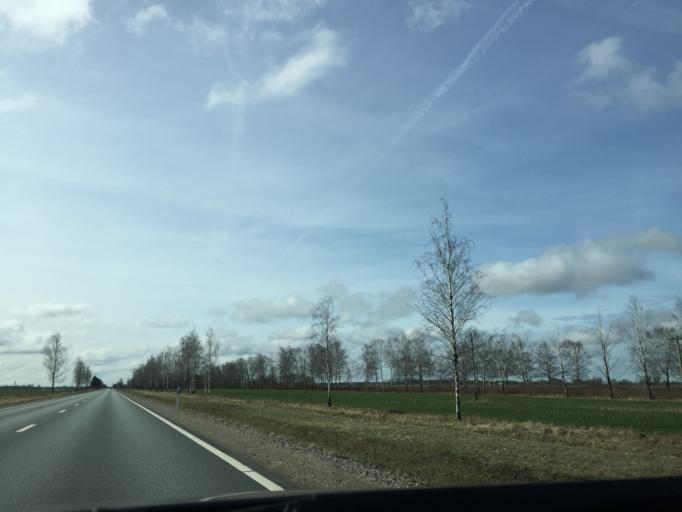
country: LV
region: Jelgava
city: Jelgava
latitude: 56.4773
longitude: 23.6954
